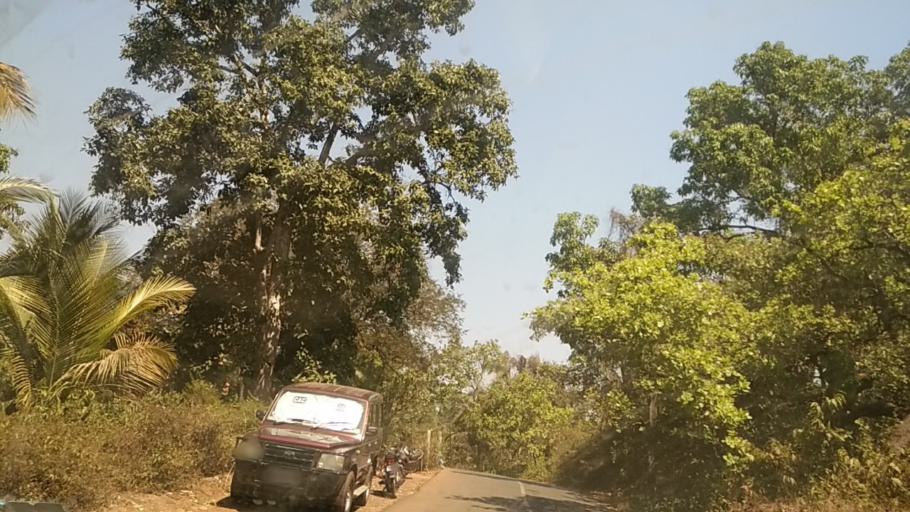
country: IN
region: Goa
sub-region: North Goa
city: Aldona
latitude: 15.5739
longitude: 73.9067
